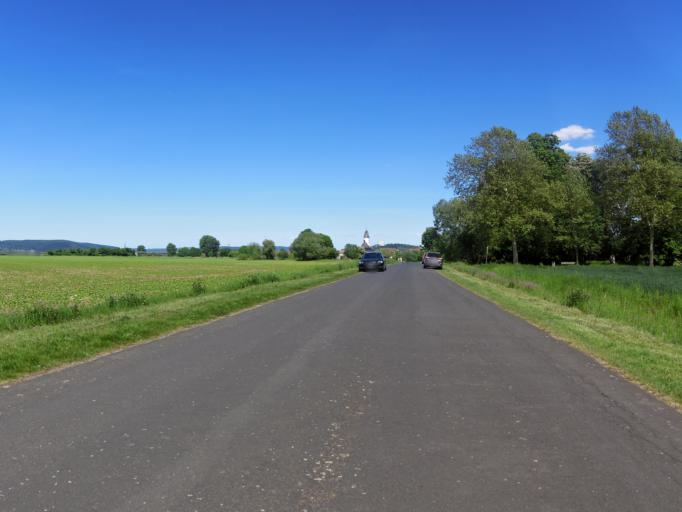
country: DE
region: North Rhine-Westphalia
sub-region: Regierungsbezirk Detmold
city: Hoexter
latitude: 51.7898
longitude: 9.4140
